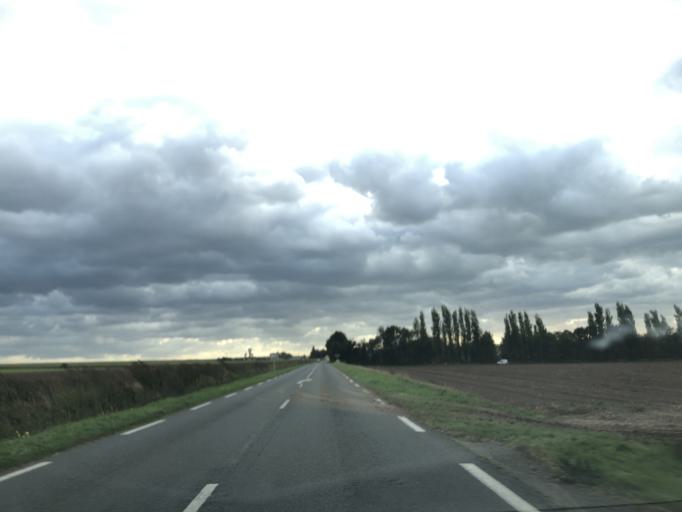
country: FR
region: Picardie
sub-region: Departement de la Somme
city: Pende
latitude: 50.1476
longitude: 1.5399
